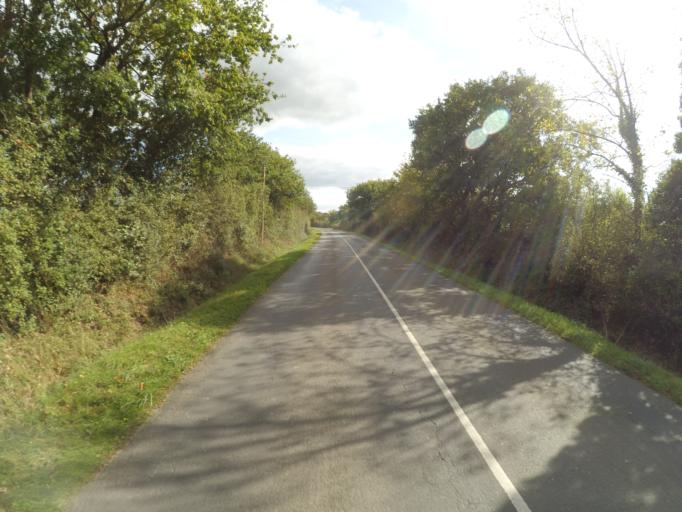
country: FR
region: Pays de la Loire
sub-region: Departement de la Loire-Atlantique
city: Casson
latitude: 47.4063
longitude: -1.5920
